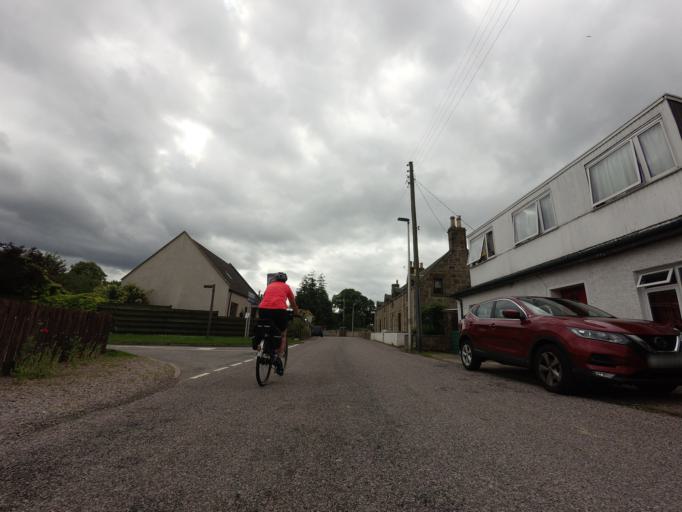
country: GB
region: Scotland
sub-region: Moray
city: Forres
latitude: 57.6059
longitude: -3.6923
